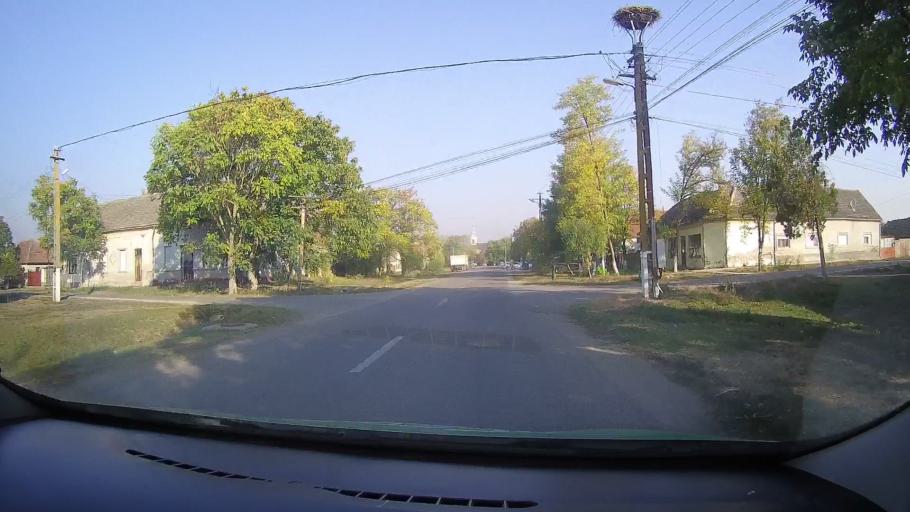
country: RO
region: Arad
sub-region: Comuna Graniceri
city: Graniceri
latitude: 46.5164
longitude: 21.3049
